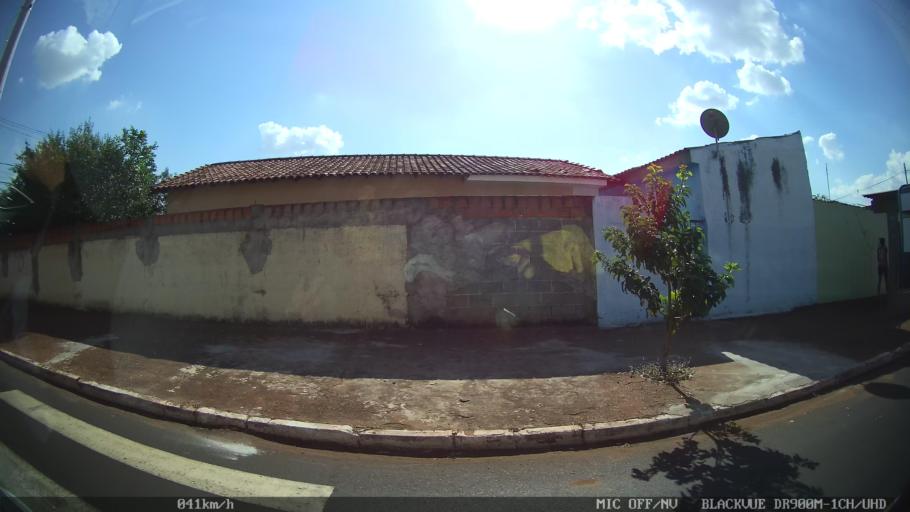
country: BR
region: Sao Paulo
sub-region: Ribeirao Preto
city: Ribeirao Preto
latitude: -21.1933
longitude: -47.8474
